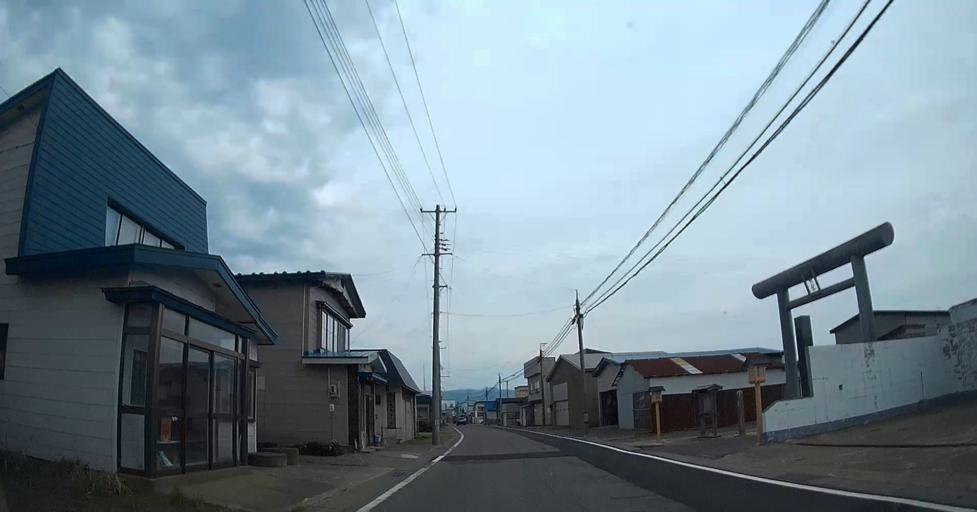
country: JP
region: Aomori
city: Shimokizukuri
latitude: 41.0326
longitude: 140.3283
